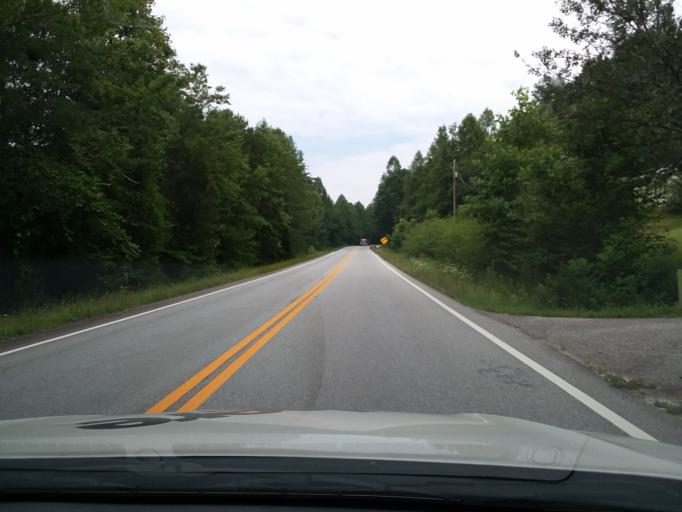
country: US
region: Georgia
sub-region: Rabun County
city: Clayton
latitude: 34.8233
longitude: -83.3207
